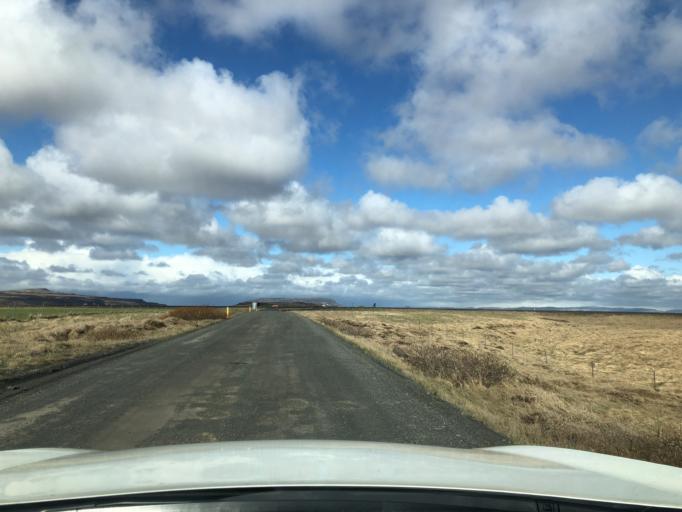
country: IS
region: South
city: Selfoss
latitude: 63.9306
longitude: -20.6702
